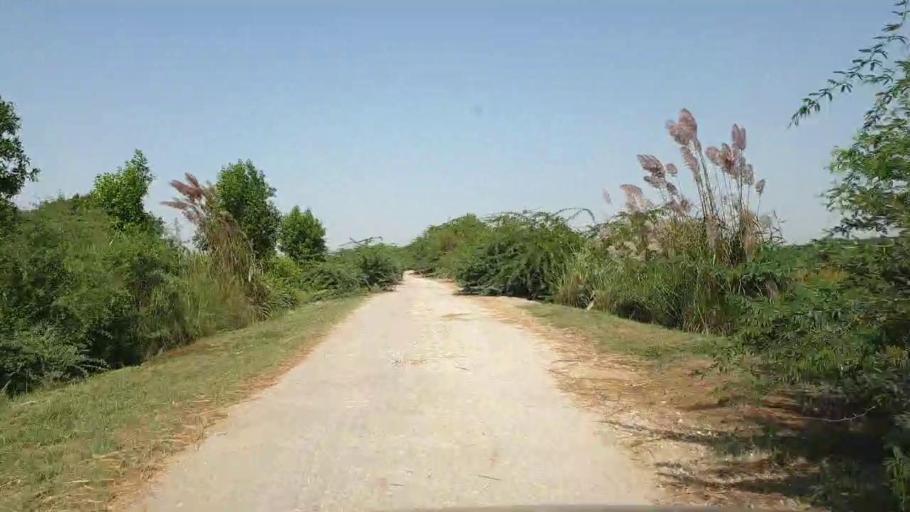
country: PK
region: Sindh
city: Tando Bago
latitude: 24.7631
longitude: 69.0233
